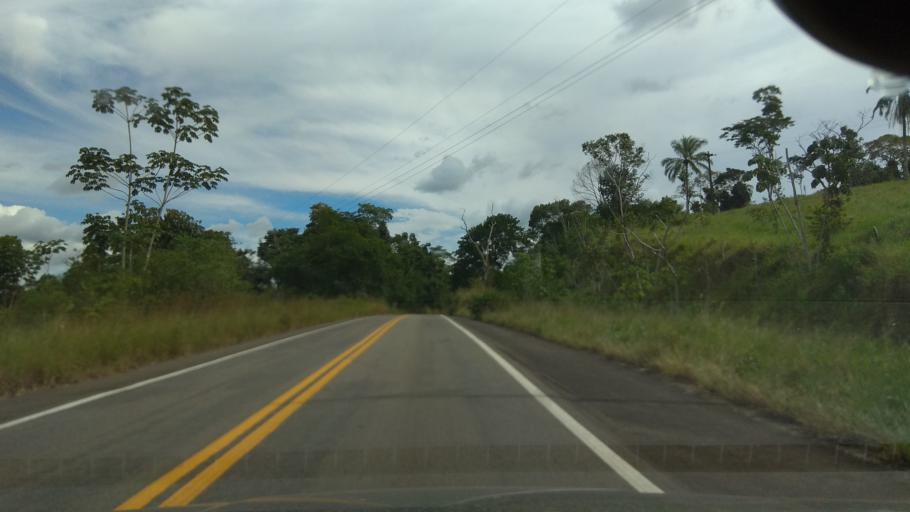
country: BR
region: Bahia
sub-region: Ubata
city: Ubata
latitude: -14.2262
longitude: -39.4707
